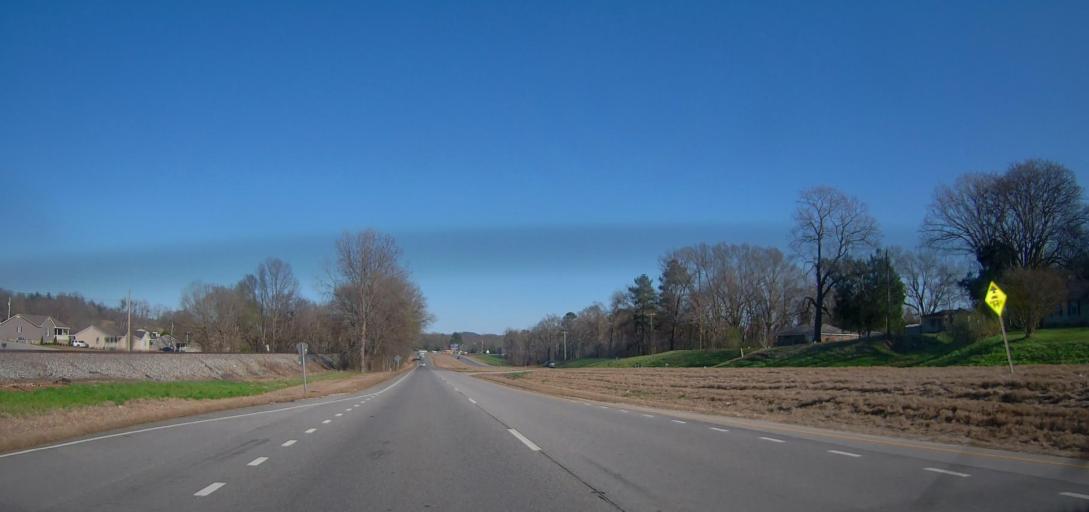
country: US
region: Alabama
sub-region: Colbert County
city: Tuscumbia
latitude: 34.7121
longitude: -87.7752
